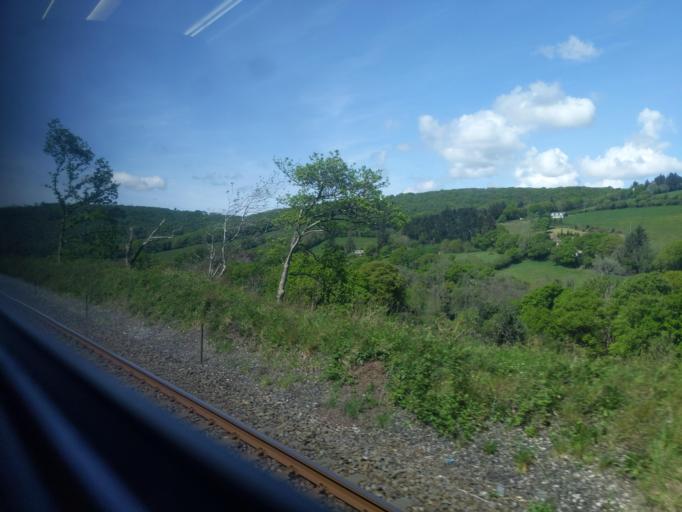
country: GB
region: England
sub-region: Cornwall
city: Lostwithiel
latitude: 50.4564
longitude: -4.6085
